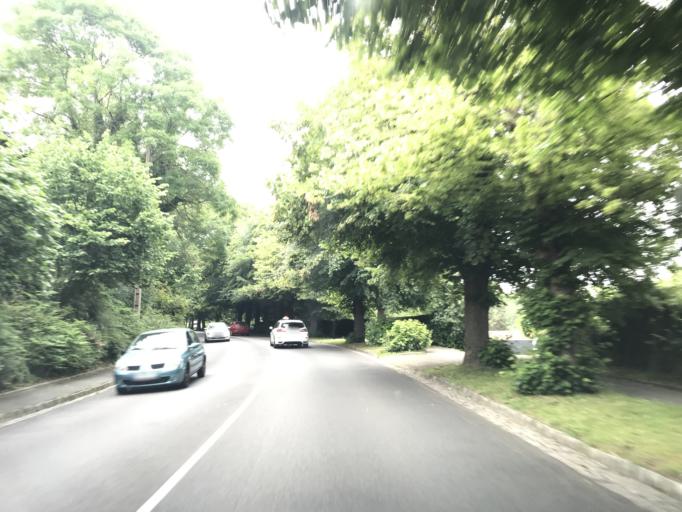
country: FR
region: Haute-Normandie
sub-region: Departement de la Seine-Maritime
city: Mont-Saint-Aignan
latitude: 49.4631
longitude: 1.0871
